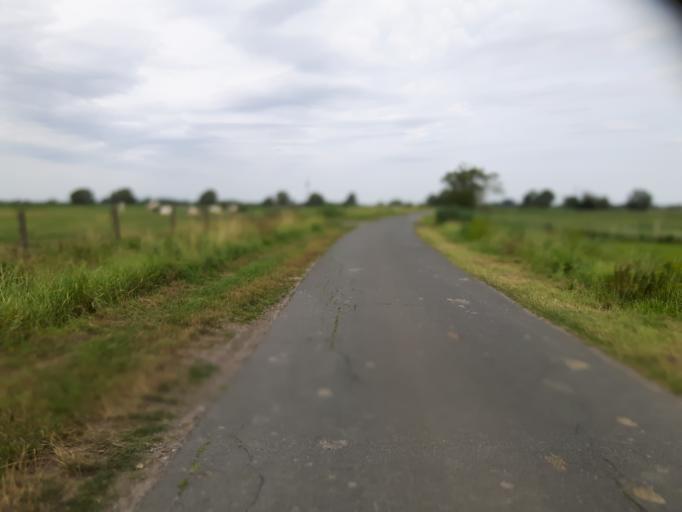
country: DE
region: Lower Saxony
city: Varel
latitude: 53.3696
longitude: 8.2087
